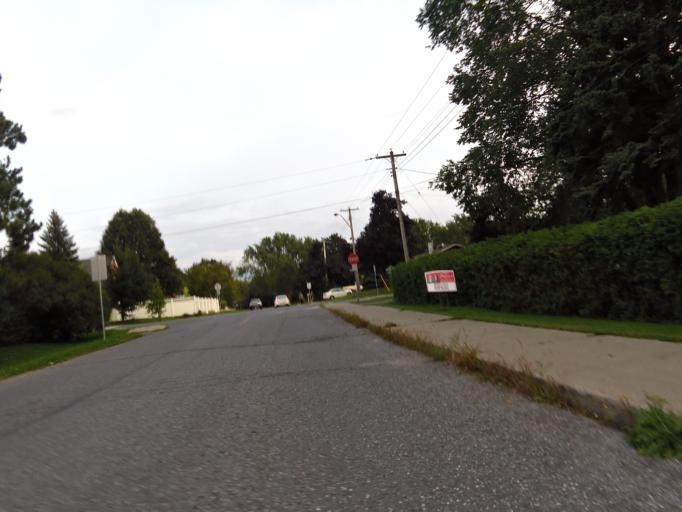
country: CA
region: Ontario
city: Bells Corners
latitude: 45.3253
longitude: -75.8224
